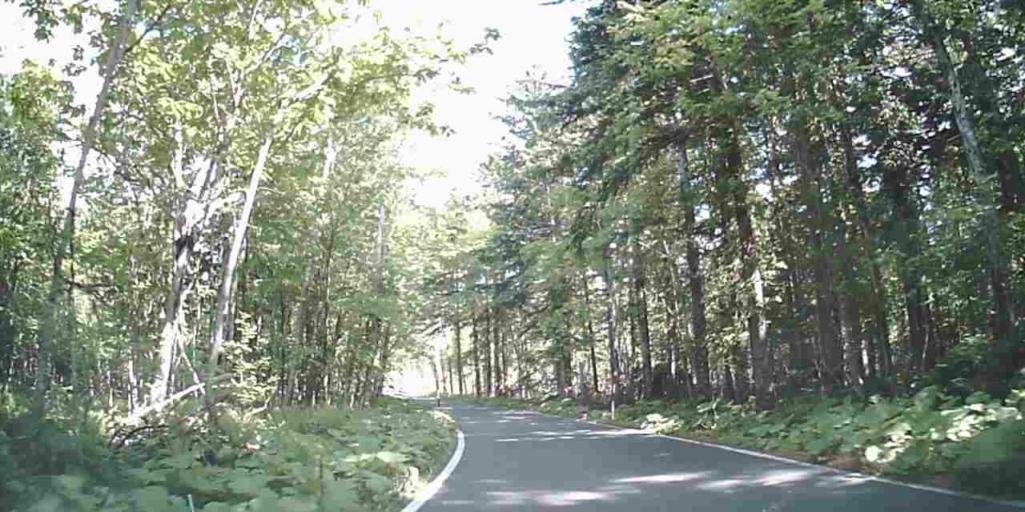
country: JP
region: Hokkaido
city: Shiraoi
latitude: 42.7336
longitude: 141.4105
